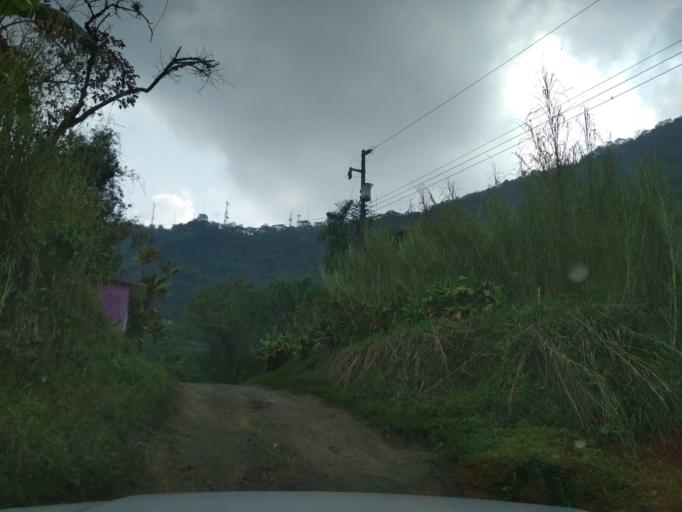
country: MX
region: Veracruz
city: Cuautlapan
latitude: 18.8675
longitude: -97.0118
